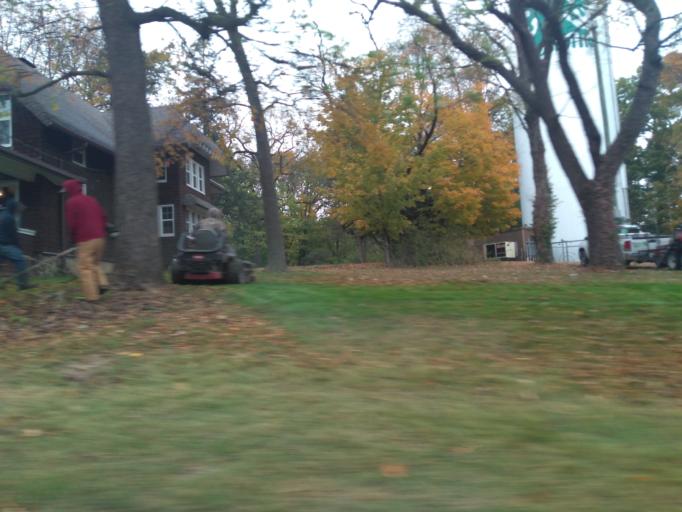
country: US
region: Illinois
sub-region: Bond County
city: Greenville
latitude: 38.8954
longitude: -89.4101
